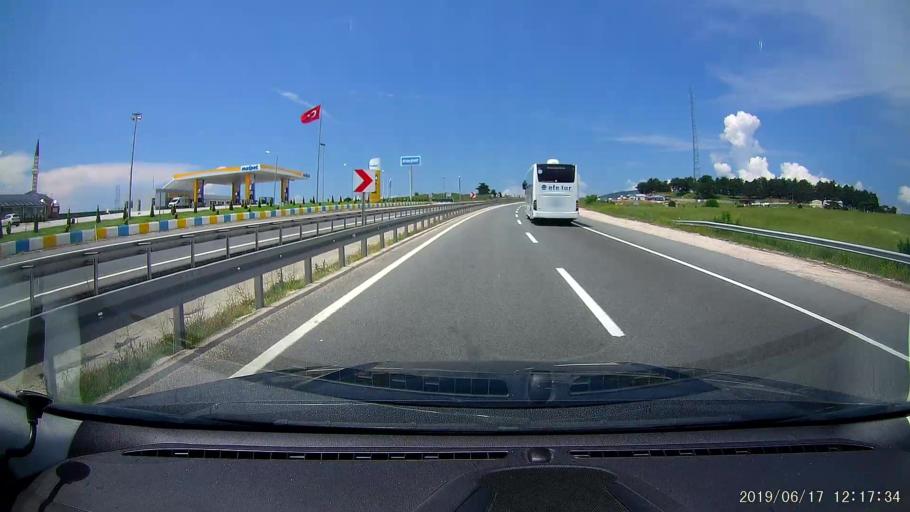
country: TR
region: Karabuk
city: Gozyeri
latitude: 40.8592
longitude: 32.5333
